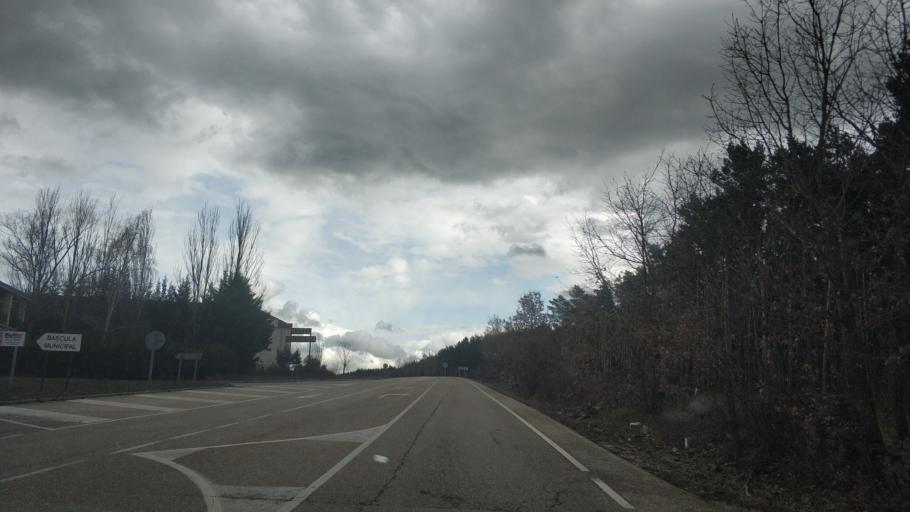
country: ES
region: Castille and Leon
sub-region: Provincia de Burgos
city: Quintanar de la Sierra
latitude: 41.9705
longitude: -3.0393
